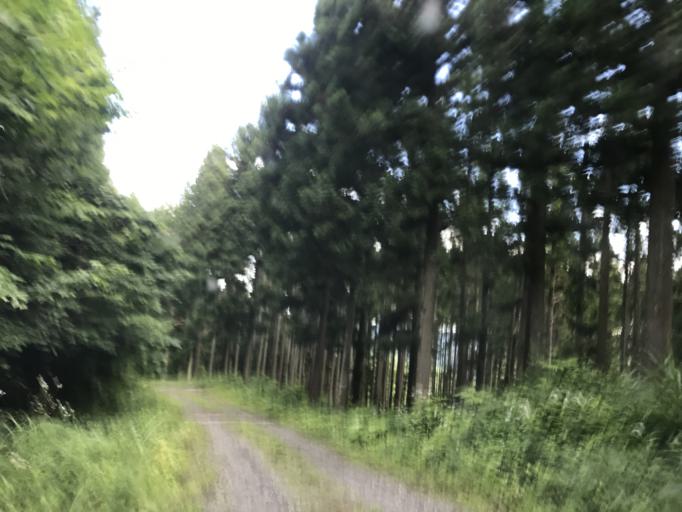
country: JP
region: Iwate
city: Ichinoseki
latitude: 38.9000
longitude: 140.9514
